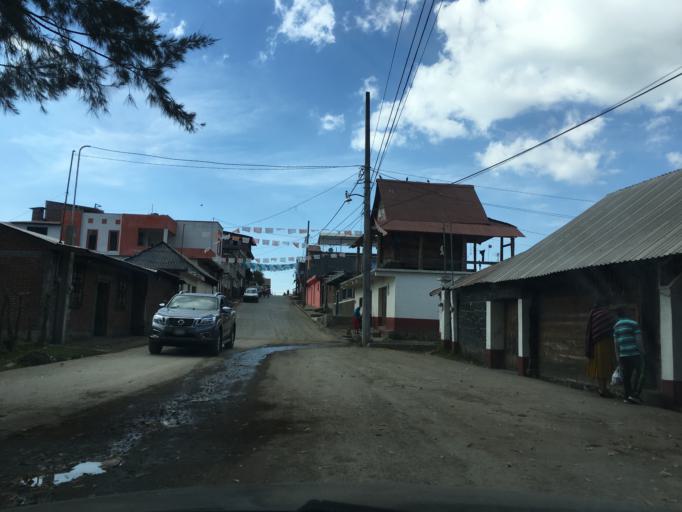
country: MX
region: Michoacan
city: Angahuan
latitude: 19.5470
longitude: -102.2222
